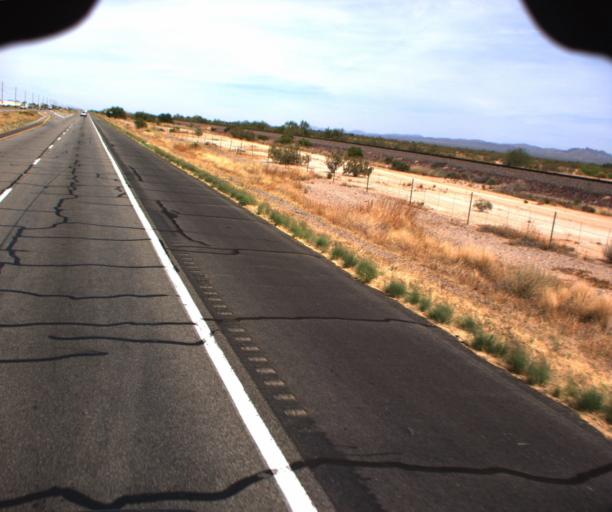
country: US
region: Arizona
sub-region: Maricopa County
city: Sun City West
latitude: 33.7601
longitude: -112.5056
